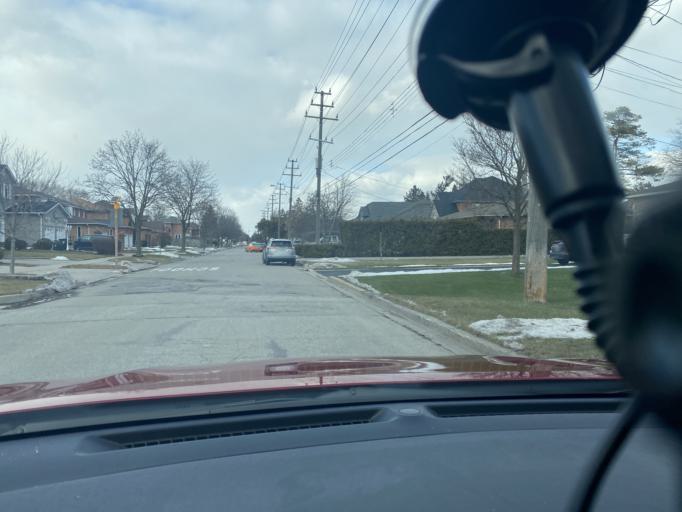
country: CA
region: Ontario
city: Scarborough
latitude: 43.7952
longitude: -79.1754
